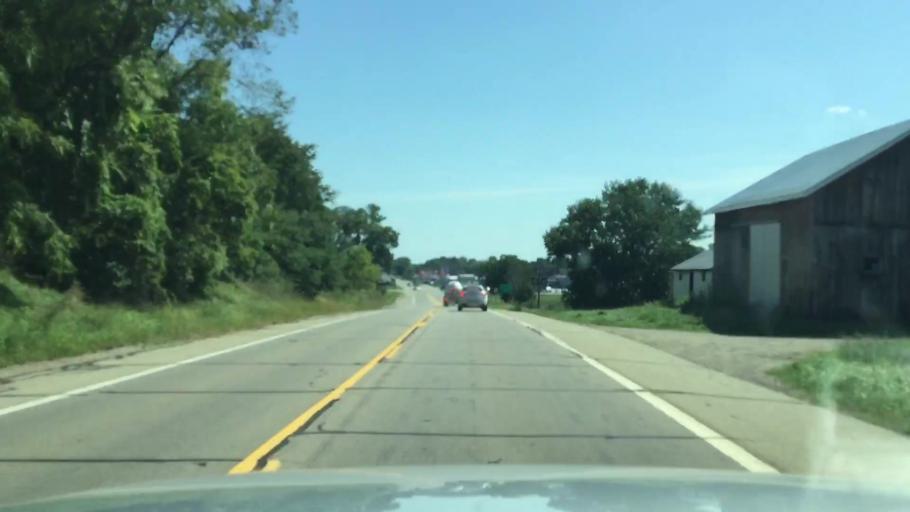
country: US
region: Michigan
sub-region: Lenawee County
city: Clinton
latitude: 42.0720
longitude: -84.0172
